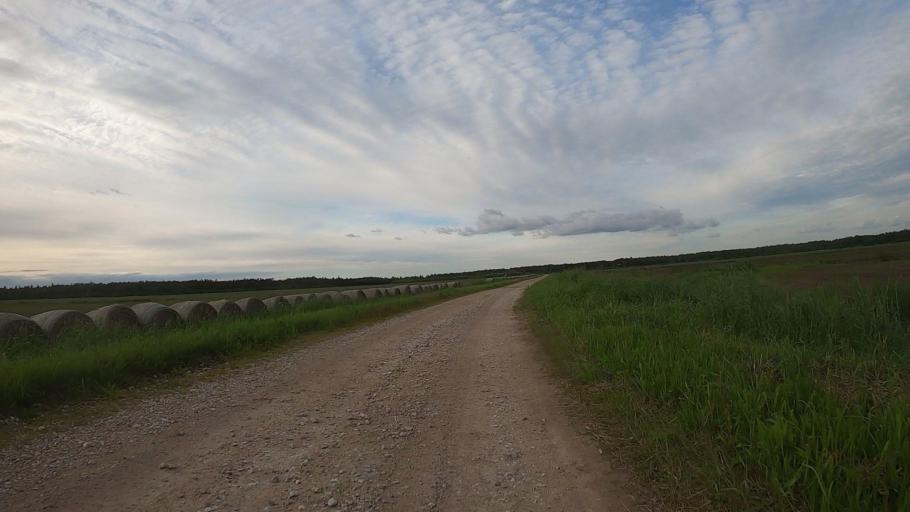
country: LV
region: Olaine
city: Olaine
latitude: 56.8216
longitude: 23.9530
